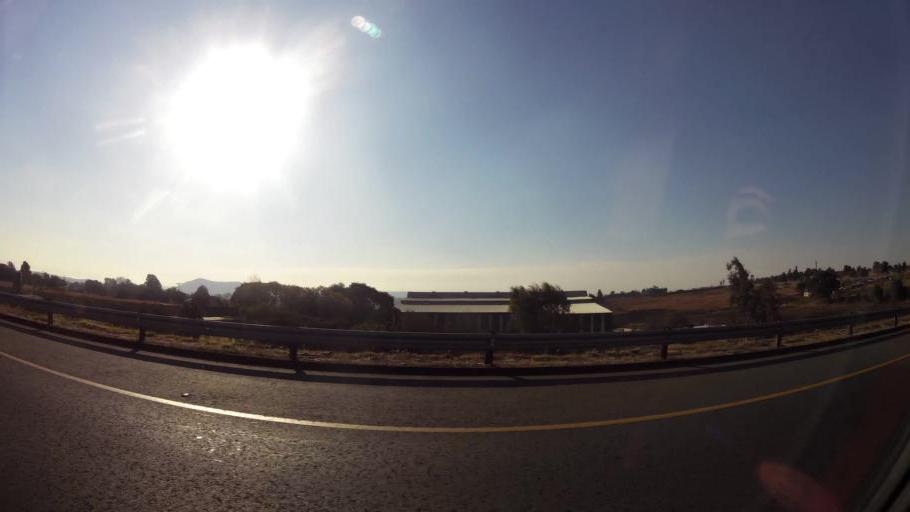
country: ZA
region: Gauteng
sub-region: West Rand District Municipality
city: Muldersdriseloop
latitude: -26.0147
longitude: 27.8739
